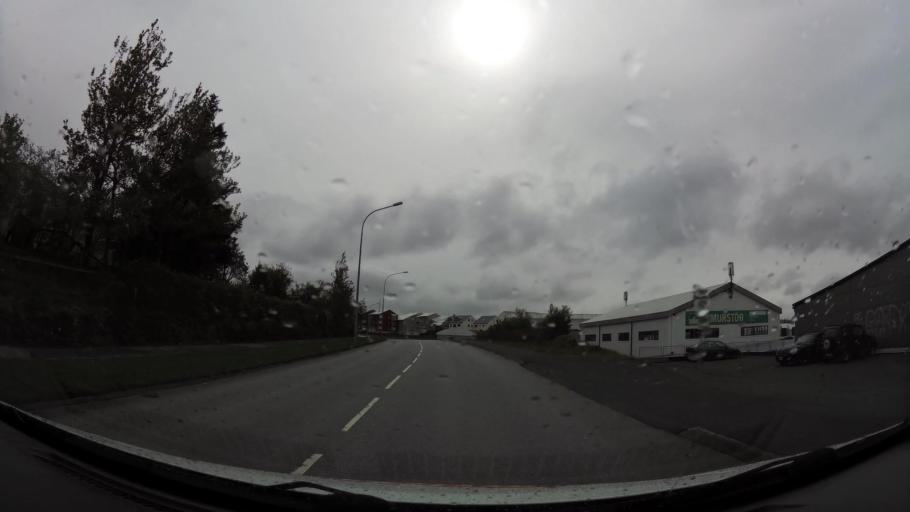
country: IS
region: Capital Region
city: Hafnarfjoerdur
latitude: 64.0576
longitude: -21.9753
